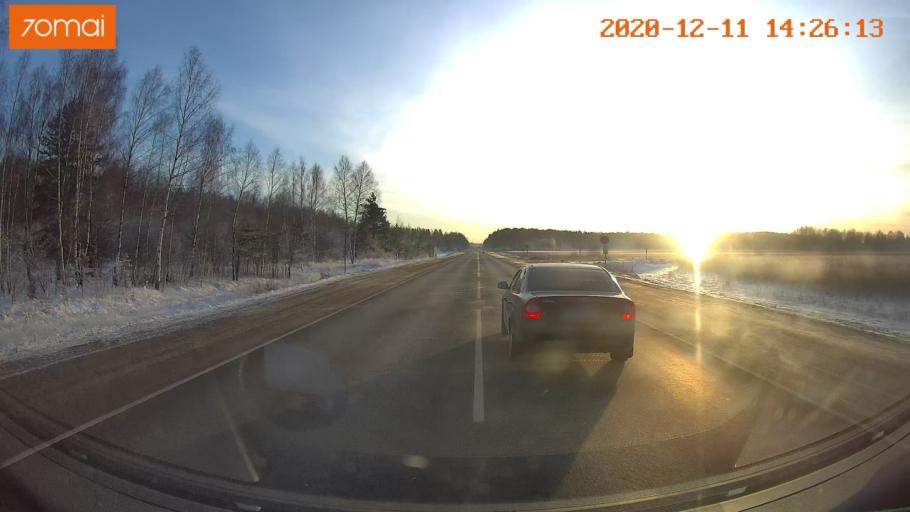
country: RU
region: Kostroma
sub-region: Kostromskoy Rayon
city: Kostroma
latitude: 57.6981
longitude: 40.8893
